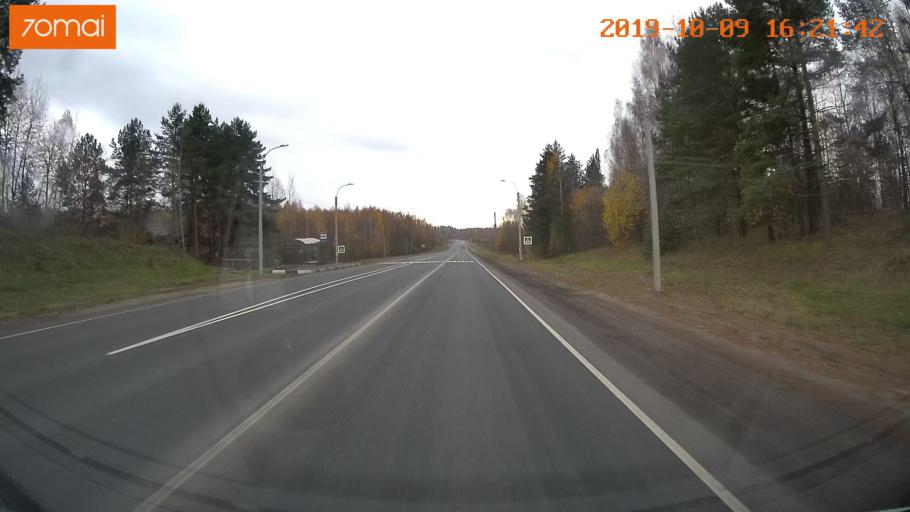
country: RU
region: Kostroma
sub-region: Kostromskoy Rayon
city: Kostroma
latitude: 57.6880
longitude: 40.8883
